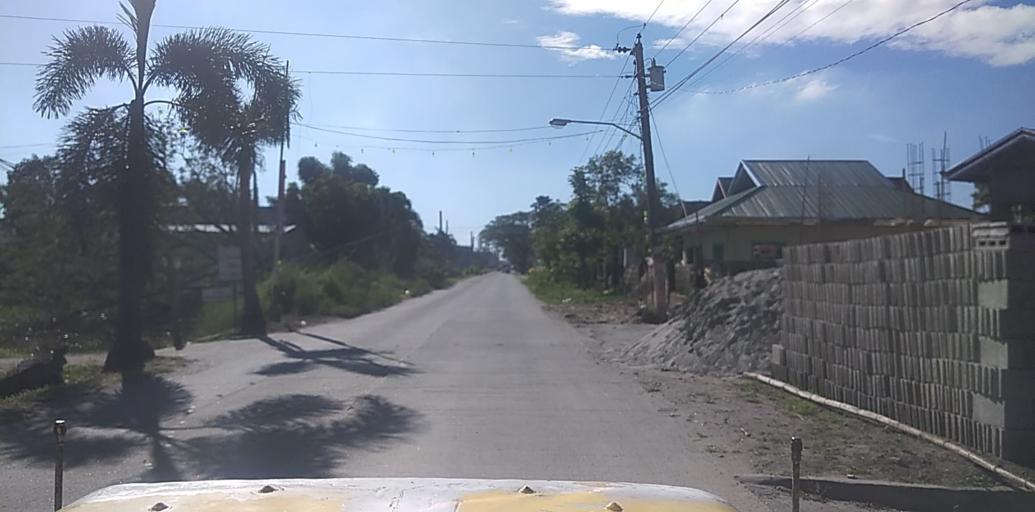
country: PH
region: Central Luzon
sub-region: Province of Pampanga
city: Mexico
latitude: 15.0764
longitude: 120.7186
